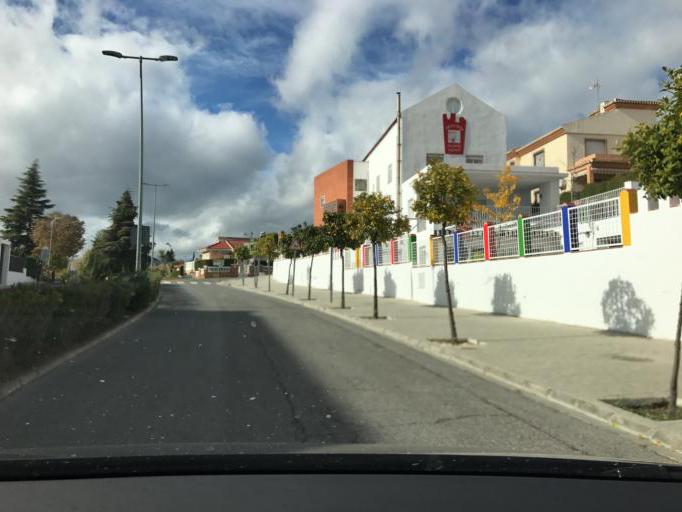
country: ES
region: Andalusia
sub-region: Provincia de Granada
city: Peligros
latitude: 37.2394
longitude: -3.6392
